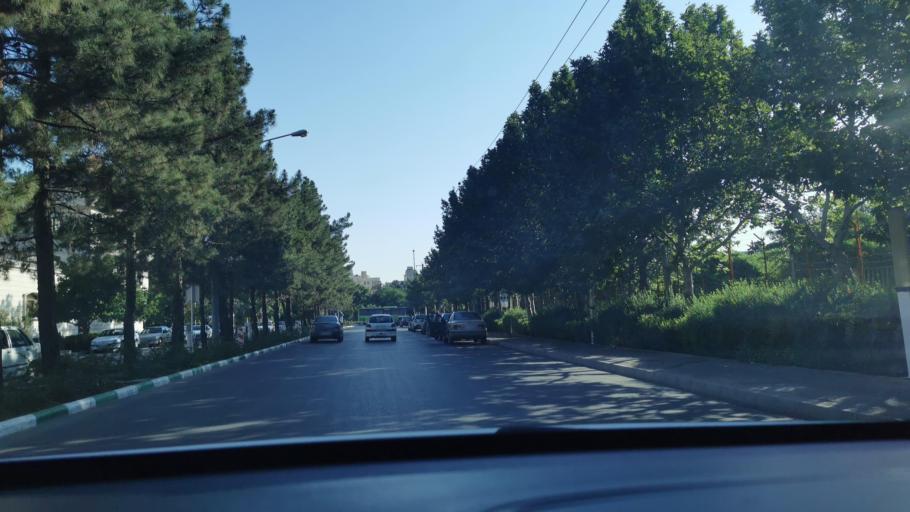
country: IR
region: Razavi Khorasan
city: Mashhad
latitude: 36.3176
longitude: 59.5270
